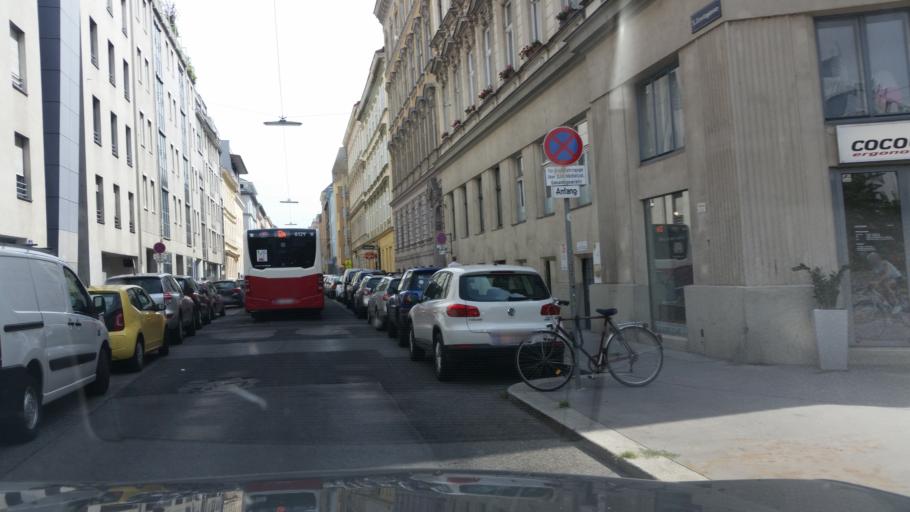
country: AT
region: Vienna
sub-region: Wien Stadt
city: Vienna
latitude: 48.1899
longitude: 16.3569
